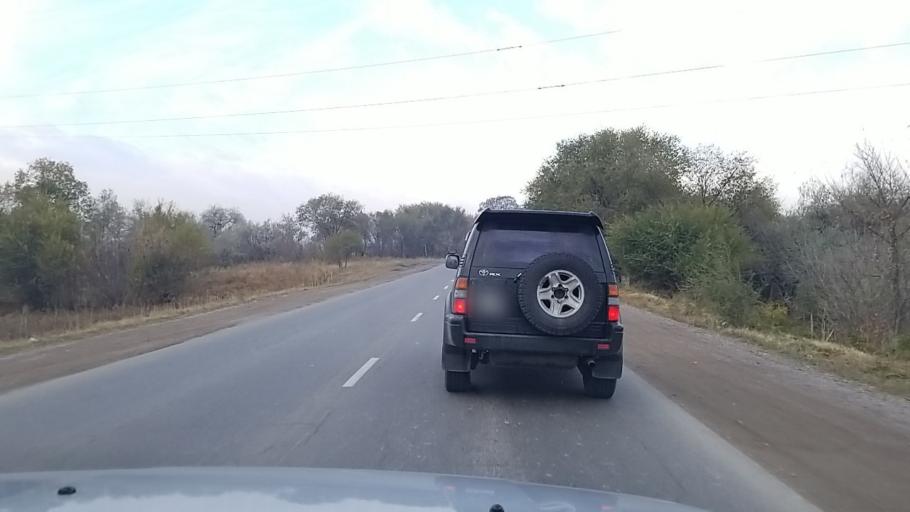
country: KZ
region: Almaty Oblysy
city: Burunday
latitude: 43.3605
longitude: 76.7449
